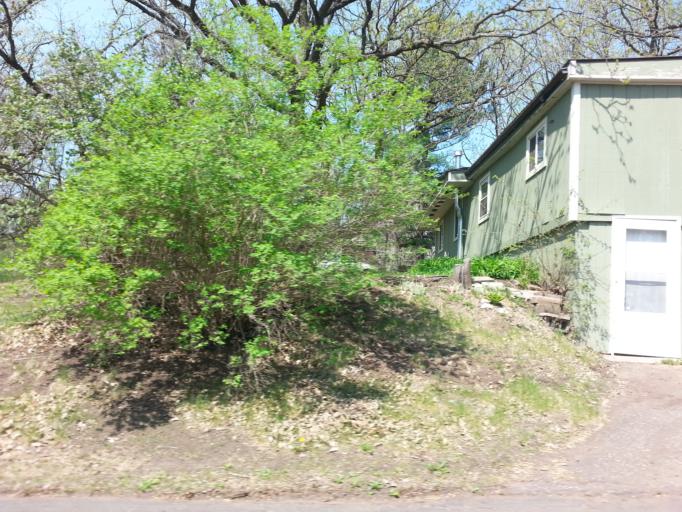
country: US
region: Minnesota
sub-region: Washington County
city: Lake Saint Croix Beach
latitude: 44.9175
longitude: -92.7735
